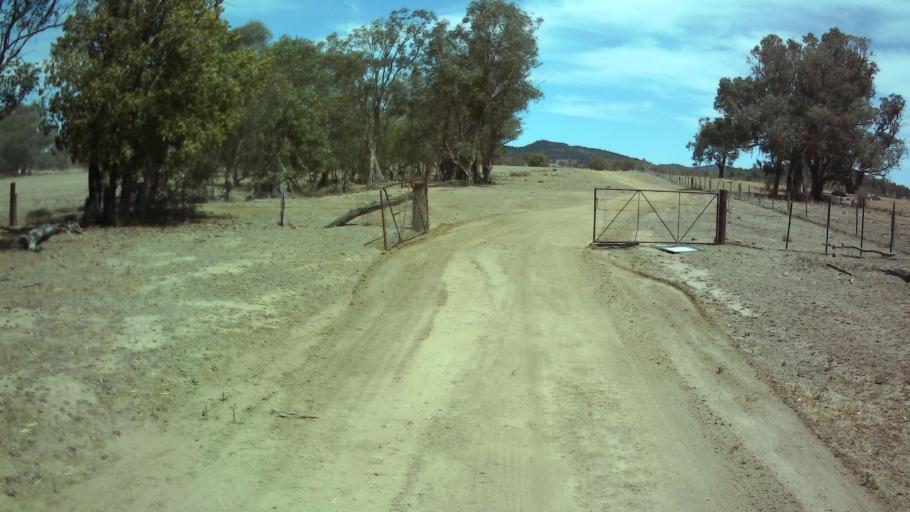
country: AU
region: New South Wales
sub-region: Weddin
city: Grenfell
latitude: -33.7670
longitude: 148.1501
